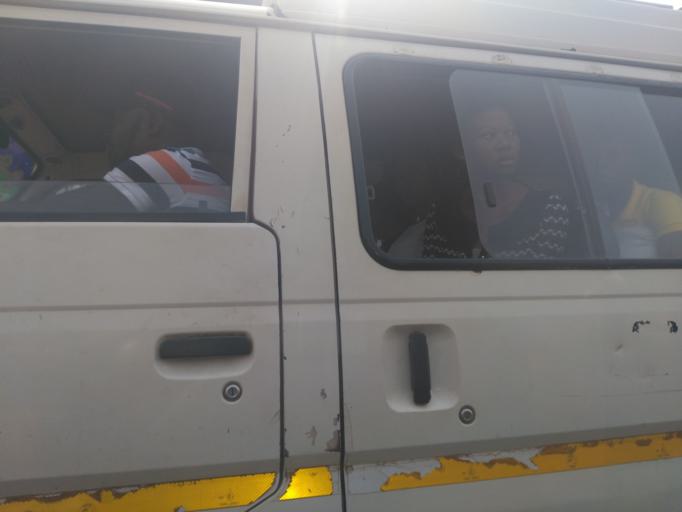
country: GH
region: Ashanti
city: Kumasi
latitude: 6.7041
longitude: -1.6341
